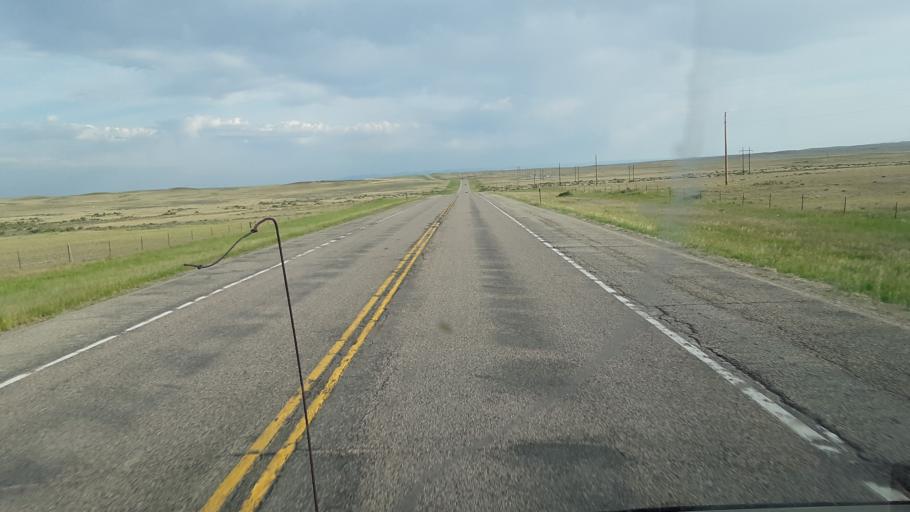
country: US
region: Wyoming
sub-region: Natrona County
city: Bar Nunn
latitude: 42.9933
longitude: -106.7100
